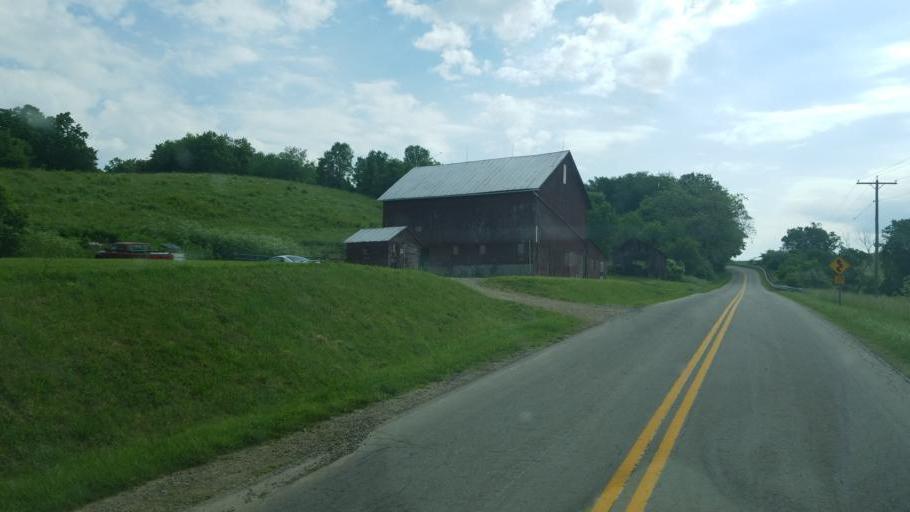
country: US
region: Ohio
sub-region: Ashland County
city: Loudonville
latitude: 40.6803
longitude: -82.2303
